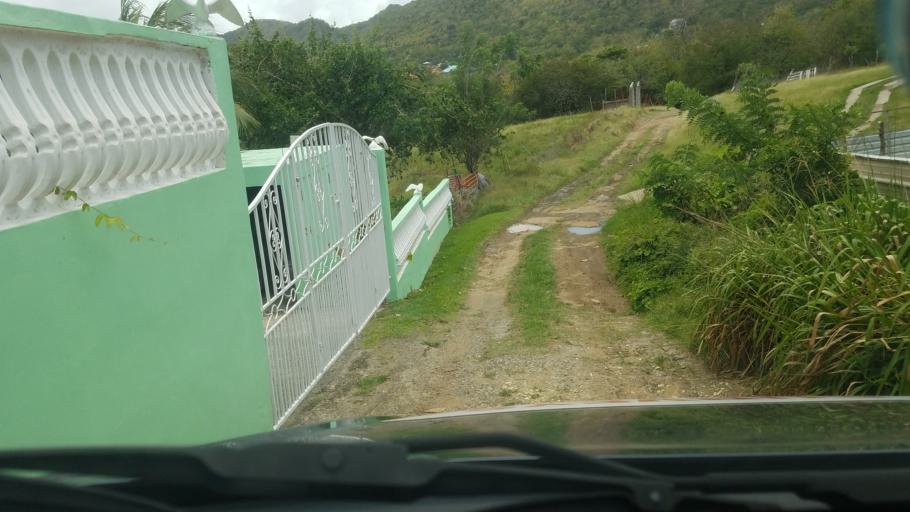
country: LC
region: Gros-Islet
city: Gros Islet
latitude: 14.0541
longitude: -60.9334
